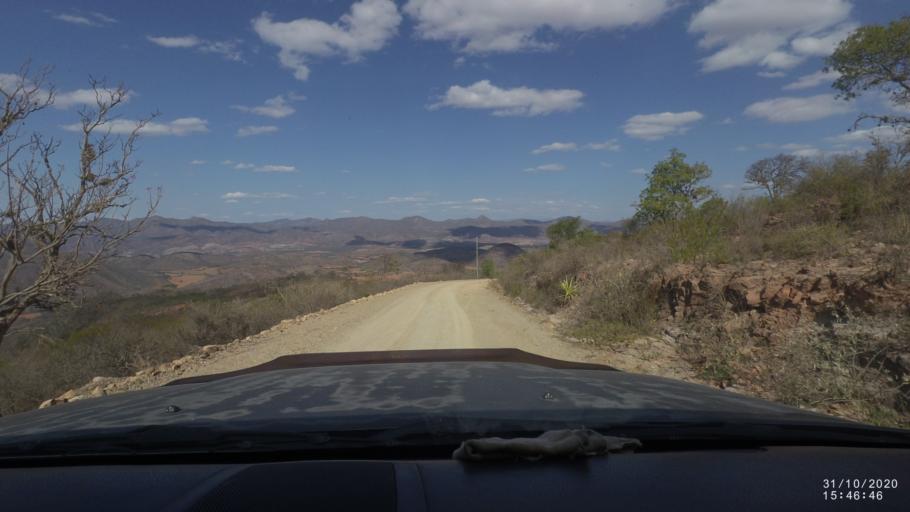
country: BO
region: Chuquisaca
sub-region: Provincia Zudanez
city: Mojocoya
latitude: -18.3149
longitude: -64.7168
